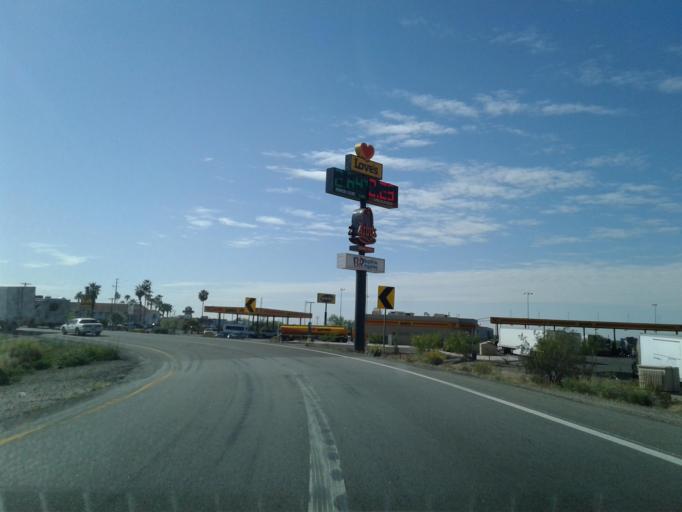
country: US
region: Arizona
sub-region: Pinal County
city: Arizona City
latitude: 32.8079
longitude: -111.6722
